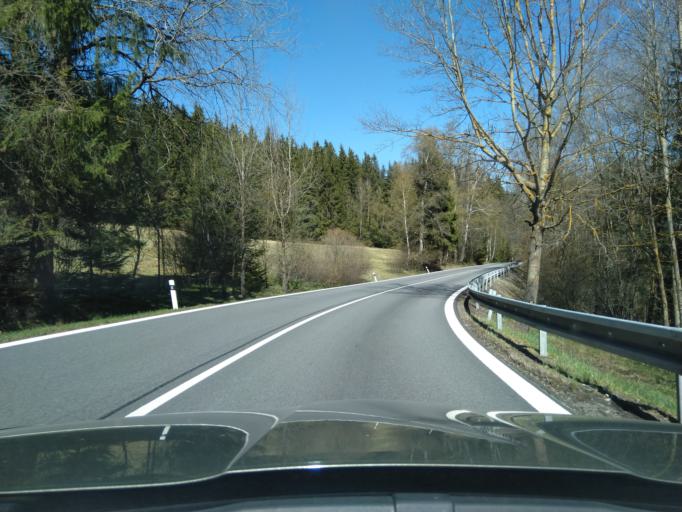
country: CZ
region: Jihocesky
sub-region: Okres Prachatice
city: Vimperk
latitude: 49.0030
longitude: 13.7651
